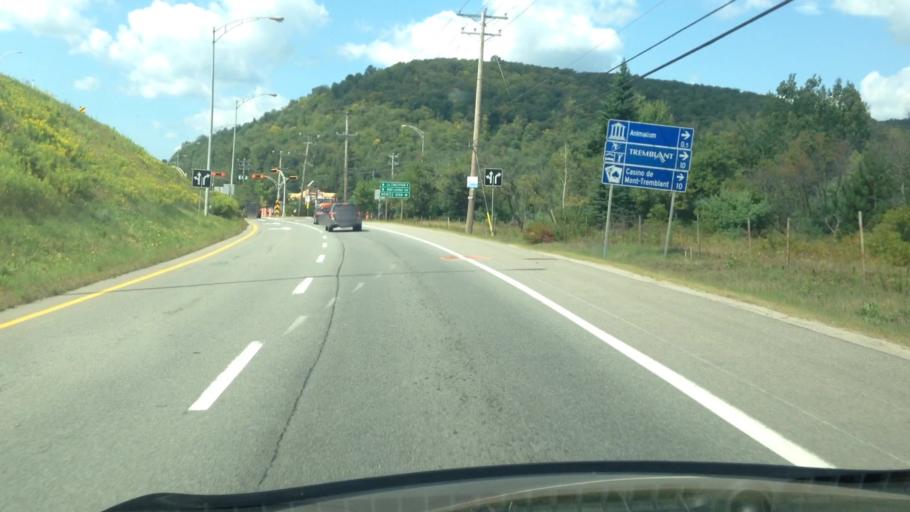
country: CA
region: Quebec
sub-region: Laurentides
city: Mont-Tremblant
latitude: 46.1323
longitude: -74.6123
